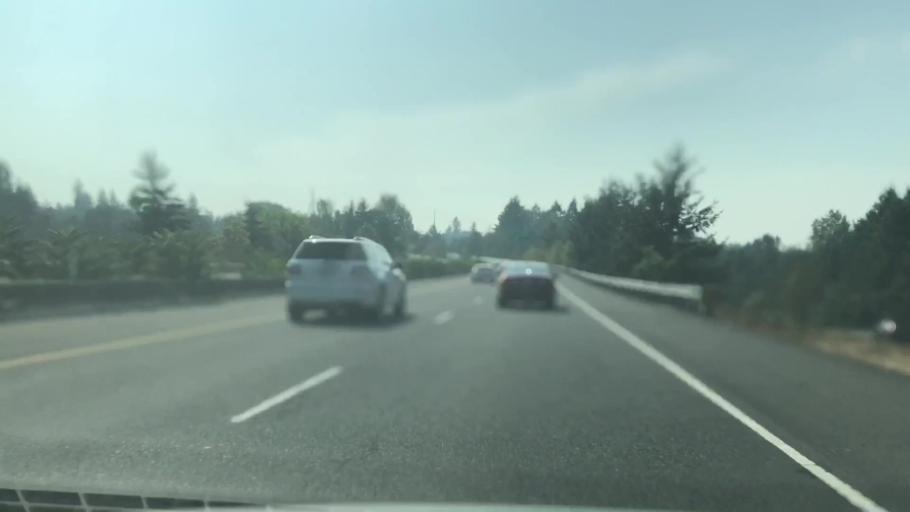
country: US
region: Washington
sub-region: Clark County
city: Minnehaha
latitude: 45.6483
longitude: -122.6445
